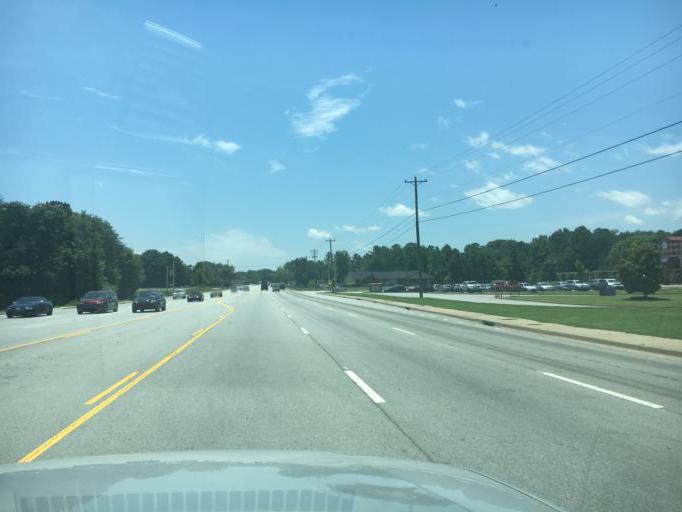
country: US
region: South Carolina
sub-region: Greenville County
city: Berea
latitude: 34.9051
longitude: -82.4614
